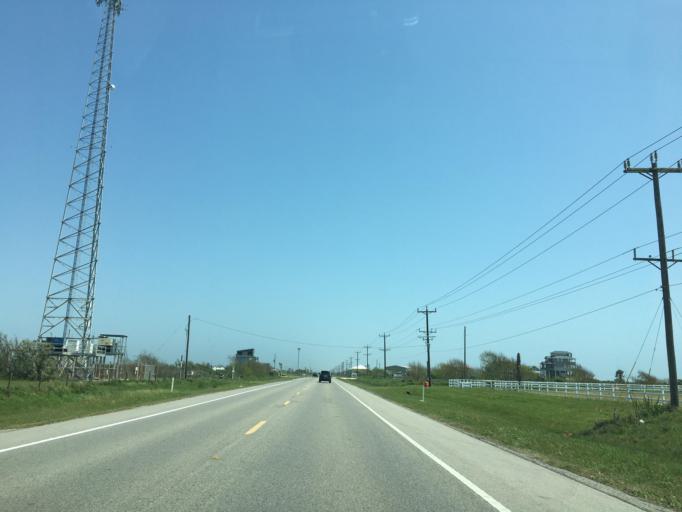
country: US
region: Texas
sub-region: Galveston County
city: Bolivar Peninsula
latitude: 29.4911
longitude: -94.5476
